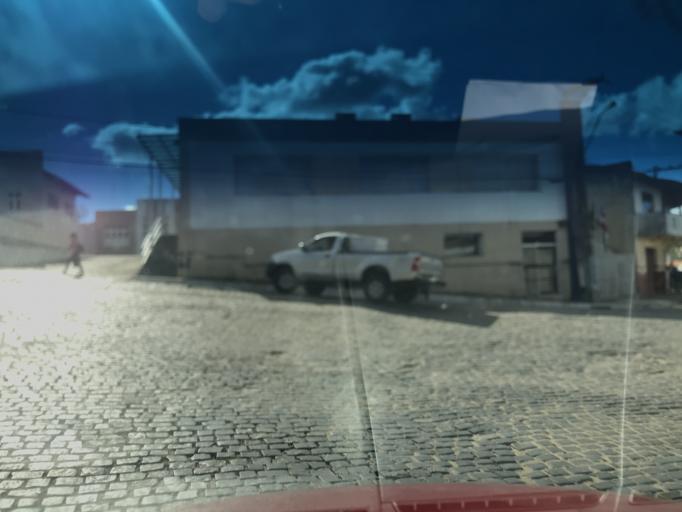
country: BR
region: Bahia
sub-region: Gandu
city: Gandu
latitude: -13.7456
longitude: -39.4891
